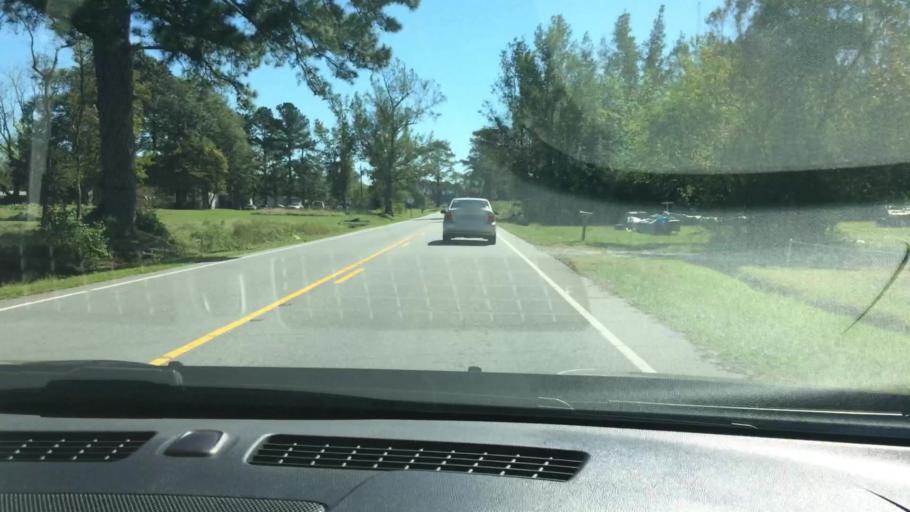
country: US
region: North Carolina
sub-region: Pitt County
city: Grifton
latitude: 35.3458
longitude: -77.3207
